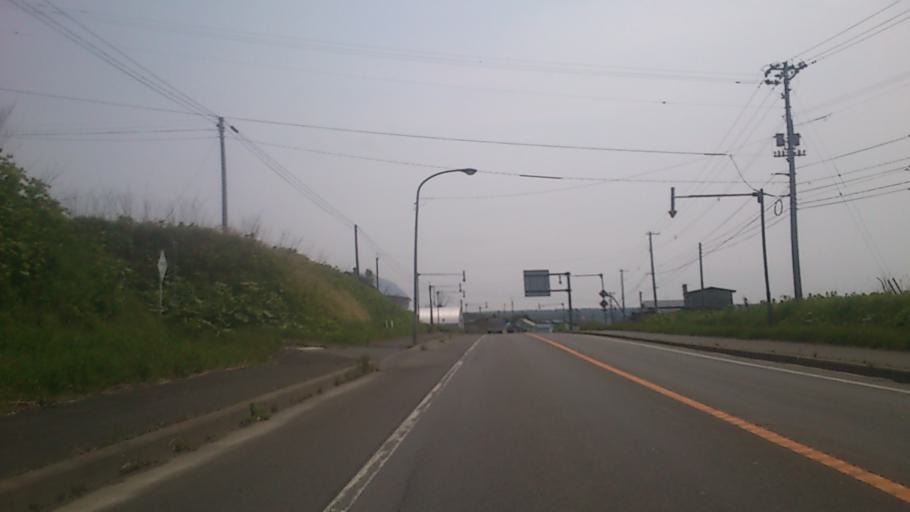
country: JP
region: Hokkaido
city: Nemuro
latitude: 43.2808
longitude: 145.5067
